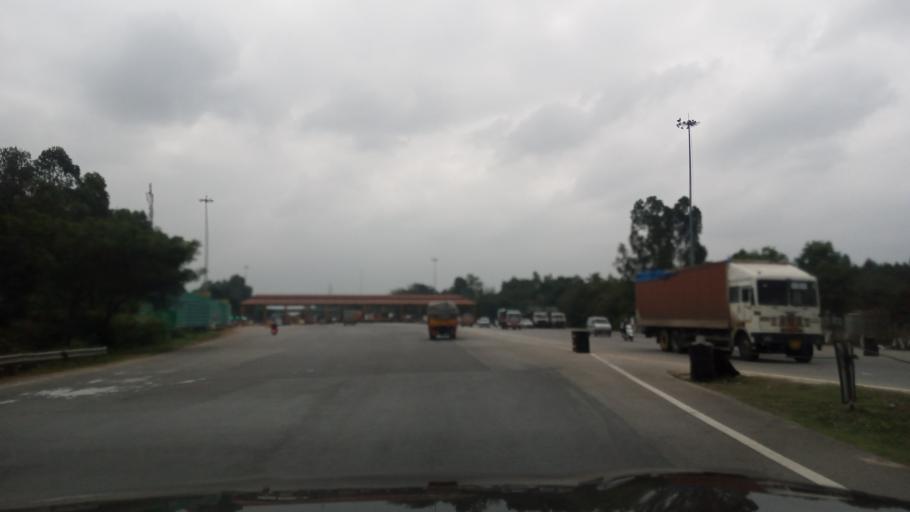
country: IN
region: Karnataka
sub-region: Bangalore Rural
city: Nelamangala
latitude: 13.0446
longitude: 77.4754
